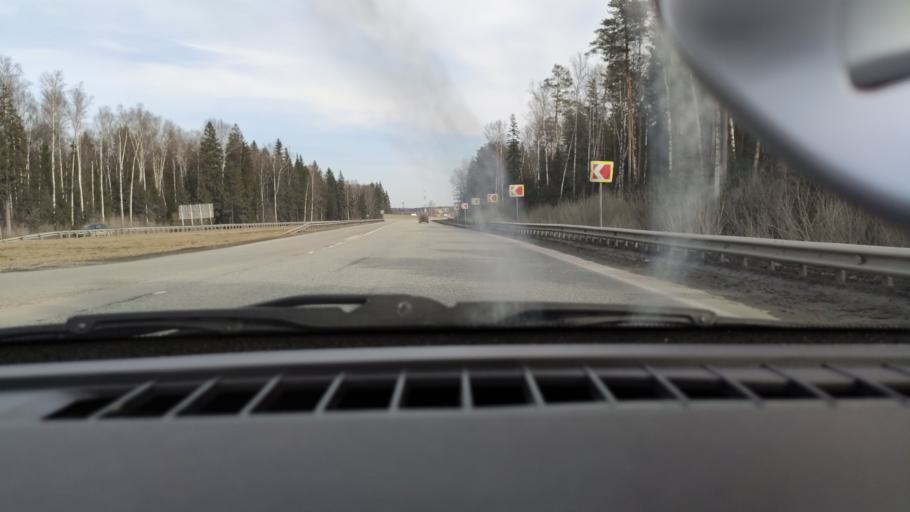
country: RU
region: Perm
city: Kondratovo
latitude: 58.0428
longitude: 56.0045
